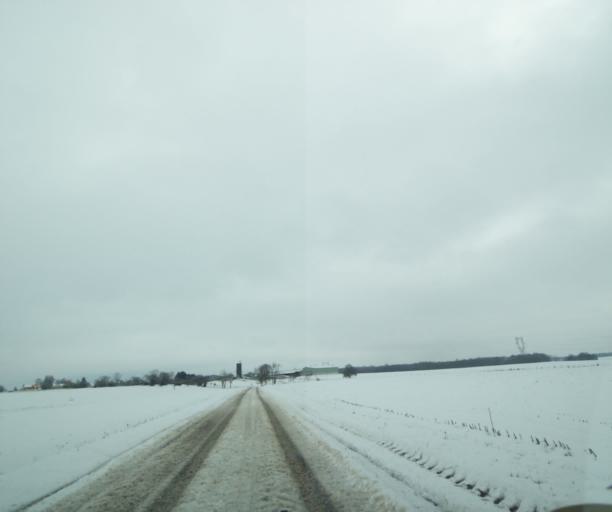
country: FR
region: Champagne-Ardenne
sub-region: Departement de la Haute-Marne
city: Montier-en-Der
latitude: 48.5138
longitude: 4.6853
